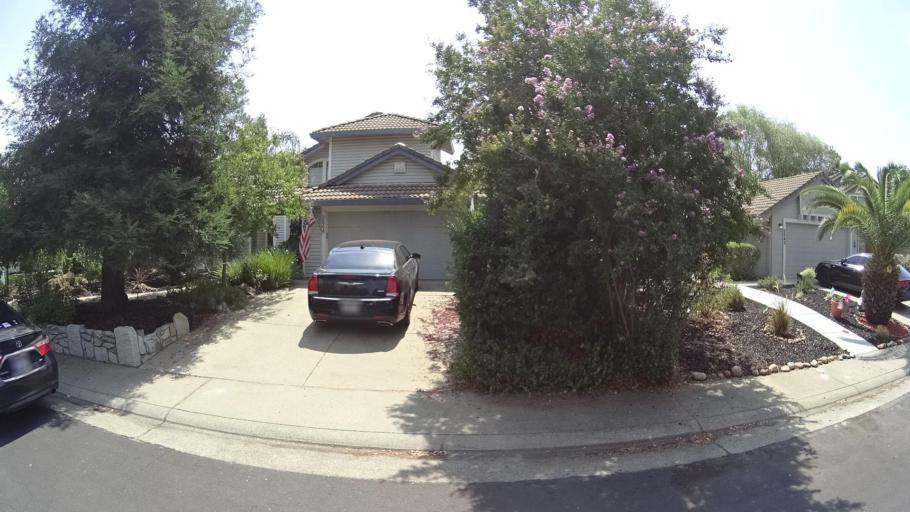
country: US
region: California
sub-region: Placer County
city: Rocklin
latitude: 38.7841
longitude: -121.2439
